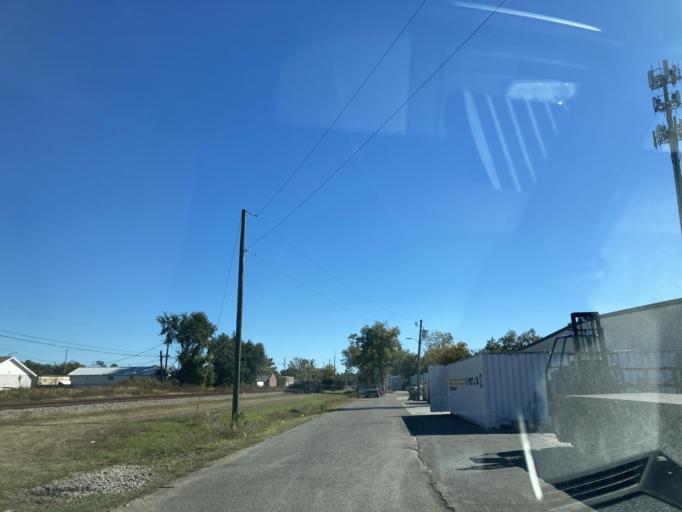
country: US
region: Mississippi
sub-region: Jackson County
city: Ocean Springs
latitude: 30.4153
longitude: -88.8222
